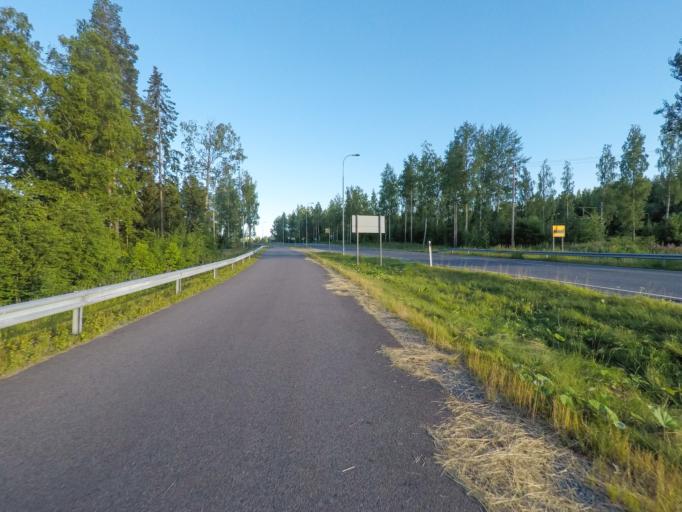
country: FI
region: Northern Savo
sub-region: Kuopio
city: Kuopio
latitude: 62.9369
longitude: 27.6679
